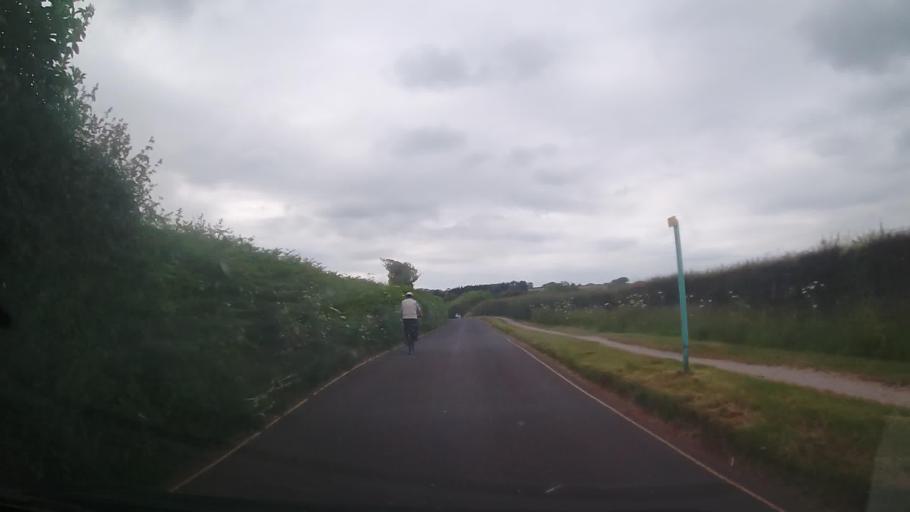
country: GB
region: England
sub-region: Devon
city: Dartmouth
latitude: 50.2890
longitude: -3.6498
